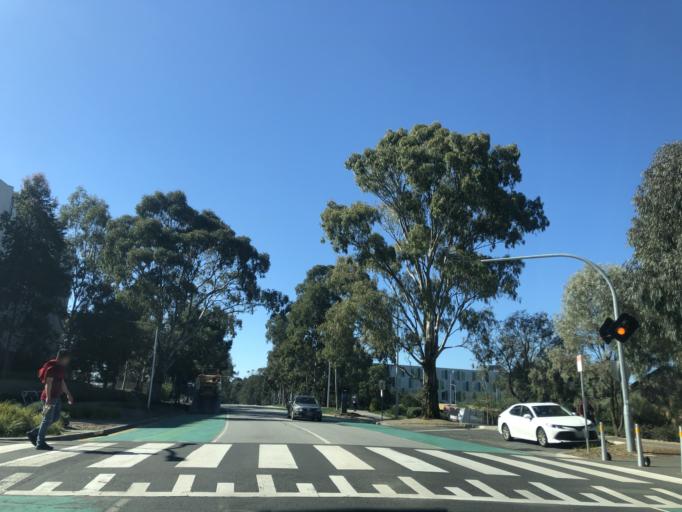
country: AU
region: Victoria
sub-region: Monash
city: Clayton
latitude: -37.9117
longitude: 145.1364
